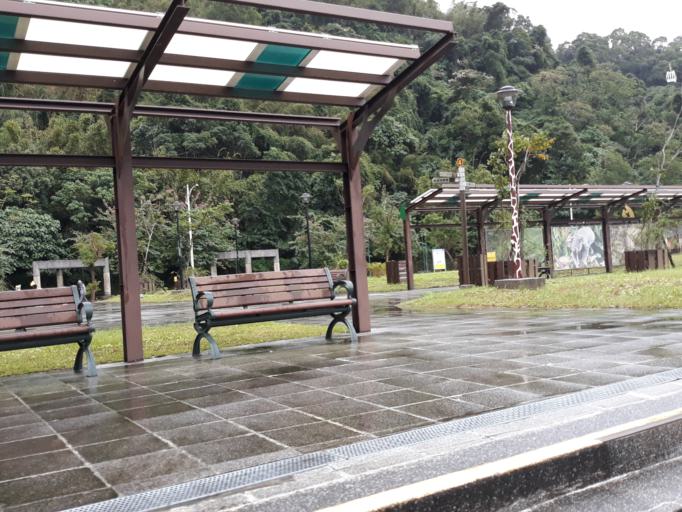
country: TW
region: Taipei
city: Taipei
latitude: 24.9970
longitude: 121.5777
